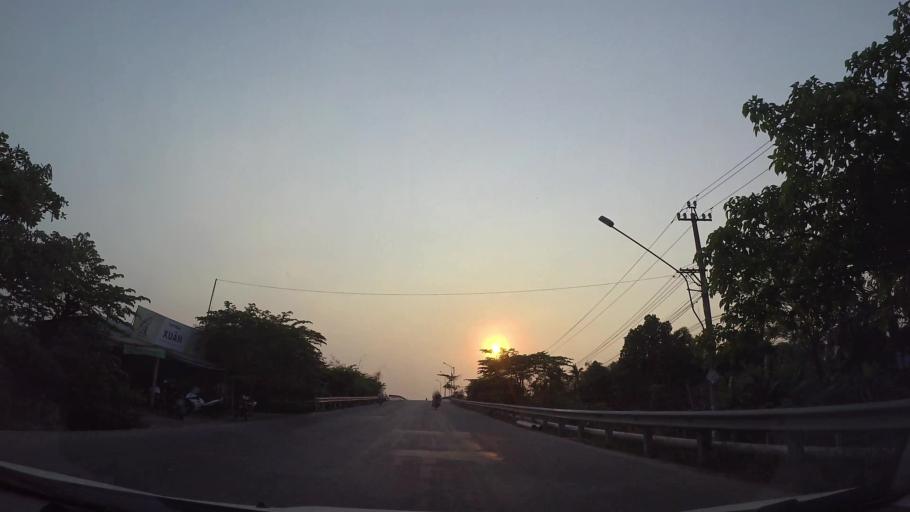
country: VN
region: Quang Nam
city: Quang Nam
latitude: 15.9478
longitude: 108.2235
